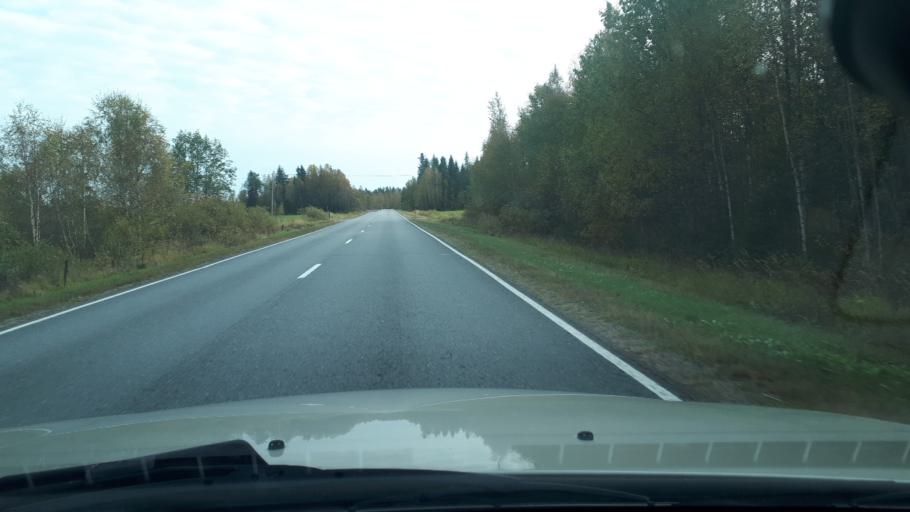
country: FI
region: Lapland
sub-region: Rovaniemi
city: Ranua
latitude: 65.9611
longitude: 26.0538
